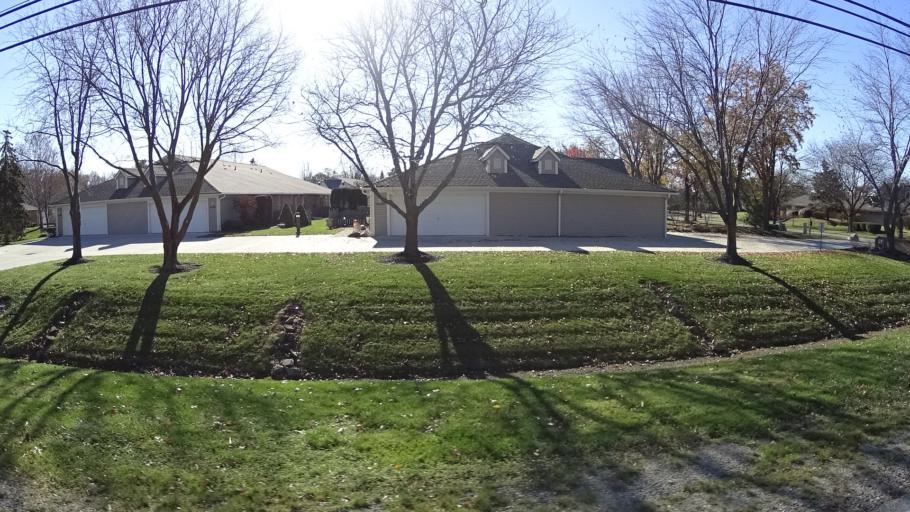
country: US
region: Ohio
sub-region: Lorain County
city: North Ridgeville
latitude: 41.4188
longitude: -82.0142
